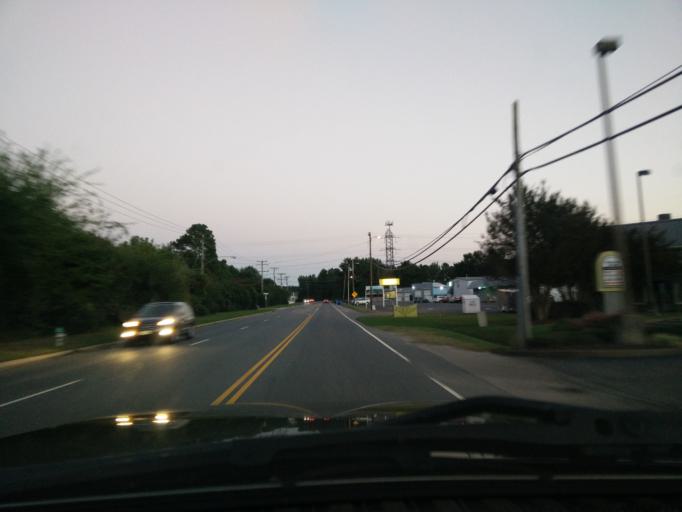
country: US
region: Virginia
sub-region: City of Chesapeake
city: Chesapeake
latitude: 36.7540
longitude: -76.2460
